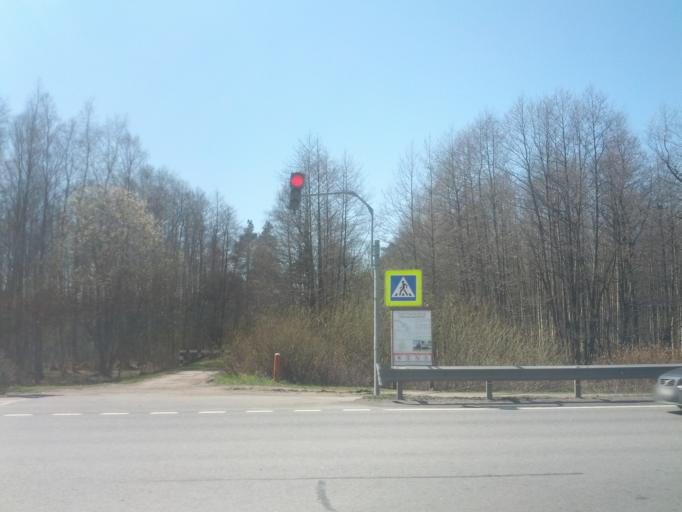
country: RU
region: St.-Petersburg
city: Razliv
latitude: 60.0759
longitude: 29.9645
